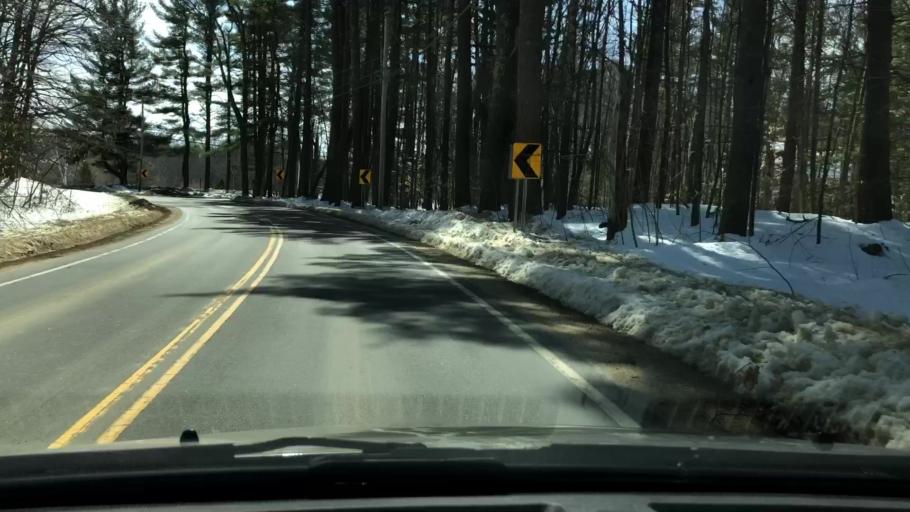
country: US
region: New Hampshire
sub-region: Strafford County
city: Madbury
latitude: 43.1693
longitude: -70.9480
